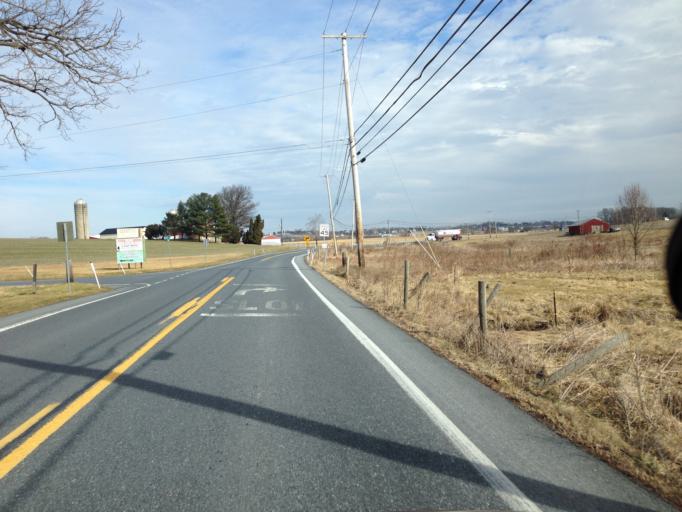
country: US
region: Pennsylvania
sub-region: Lancaster County
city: Penryn
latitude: 40.1787
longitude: -76.3604
